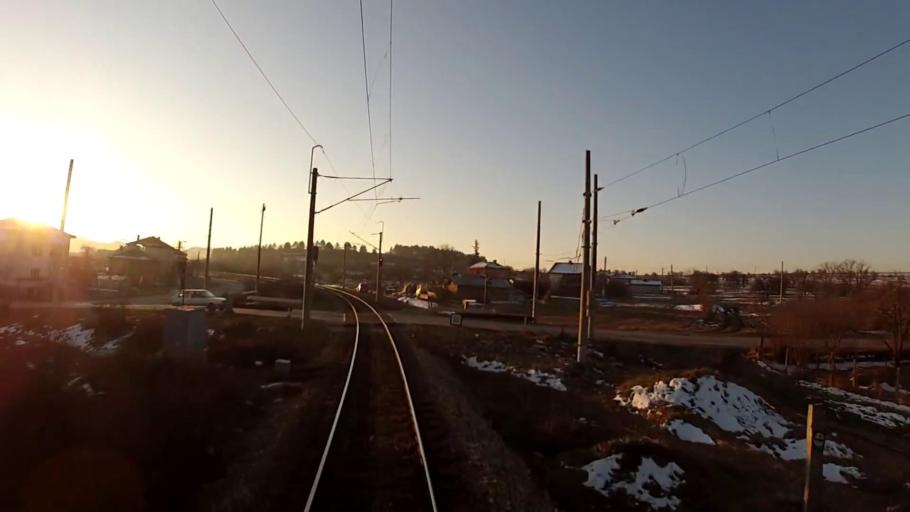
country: BG
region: Sofiya
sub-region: Obshtina Dragoman
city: Dragoman
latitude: 42.9148
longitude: 22.9369
